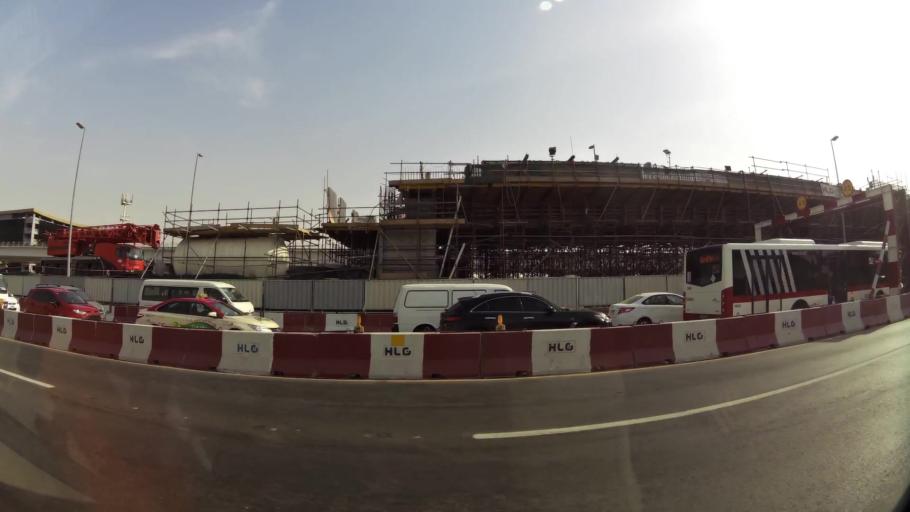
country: AE
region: Ash Shariqah
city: Sharjah
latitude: 25.2315
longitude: 55.3897
